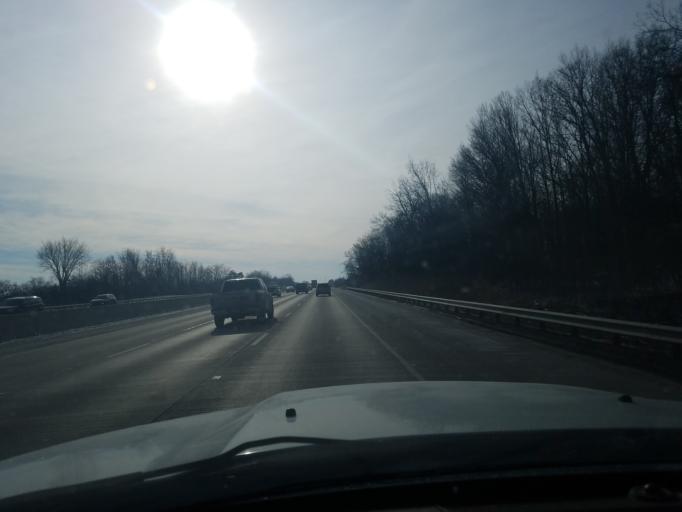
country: US
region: Indiana
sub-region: Allen County
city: Fort Wayne
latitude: 41.1086
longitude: -85.2010
